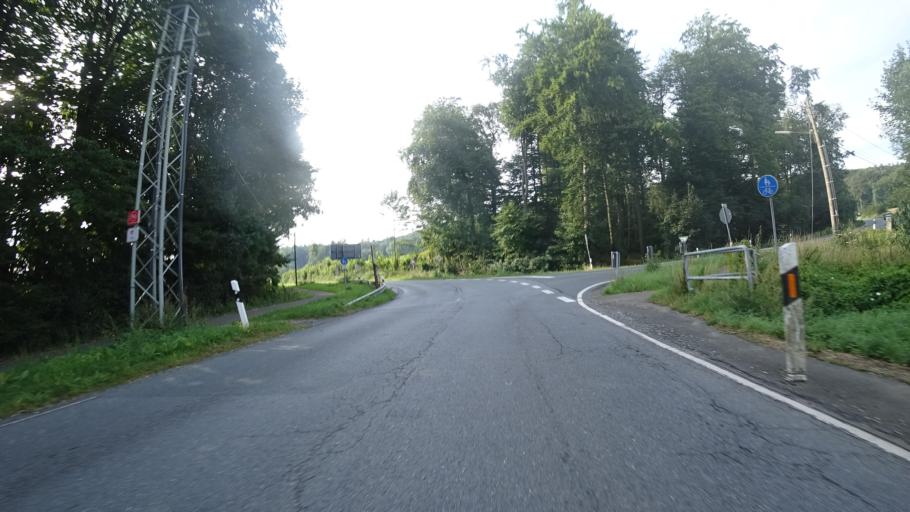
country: DE
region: North Rhine-Westphalia
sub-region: Regierungsbezirk Detmold
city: Bielefeld
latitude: 52.0231
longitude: 8.4690
